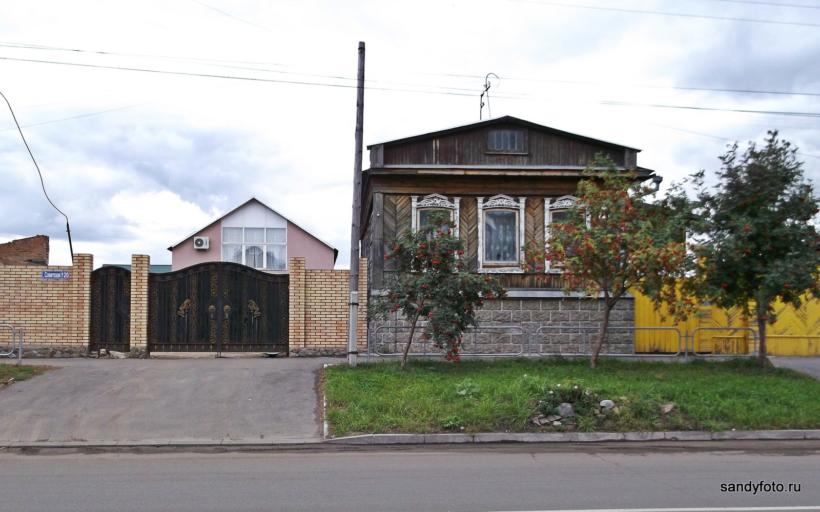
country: RU
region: Chelyabinsk
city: Troitsk
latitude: 54.0893
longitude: 61.5704
